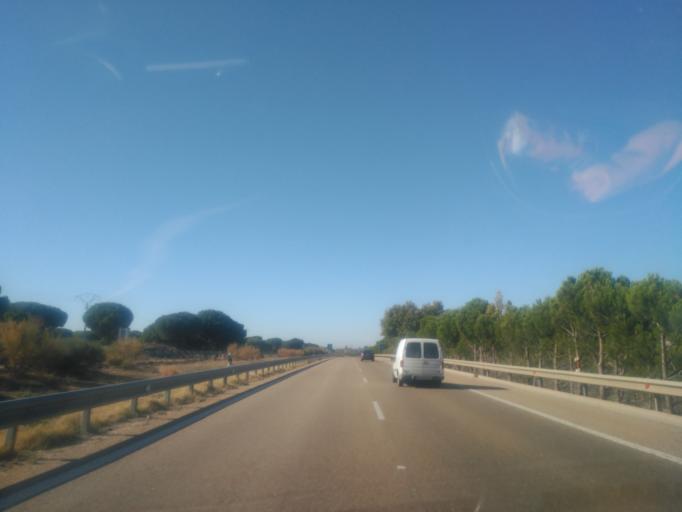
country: ES
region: Castille and Leon
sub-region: Provincia de Valladolid
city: Tudela de Duero
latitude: 41.5885
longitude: -4.5434
